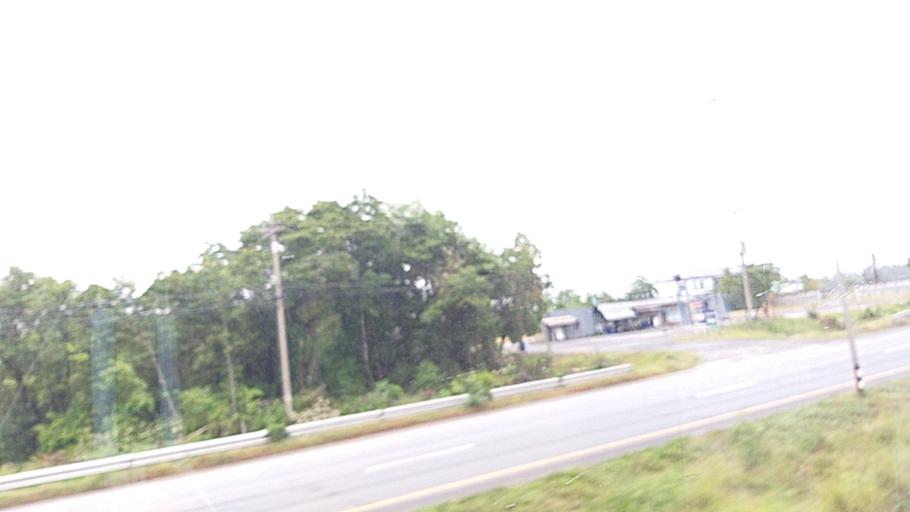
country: TH
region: Nakhon Ratchasima
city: Non Sung
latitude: 15.0969
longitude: 102.2554
